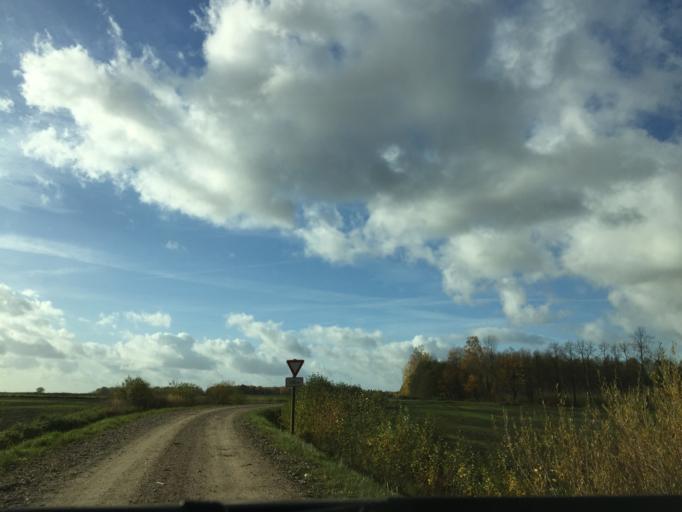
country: LV
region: Ogre
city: Jumprava
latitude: 56.7391
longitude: 24.9030
